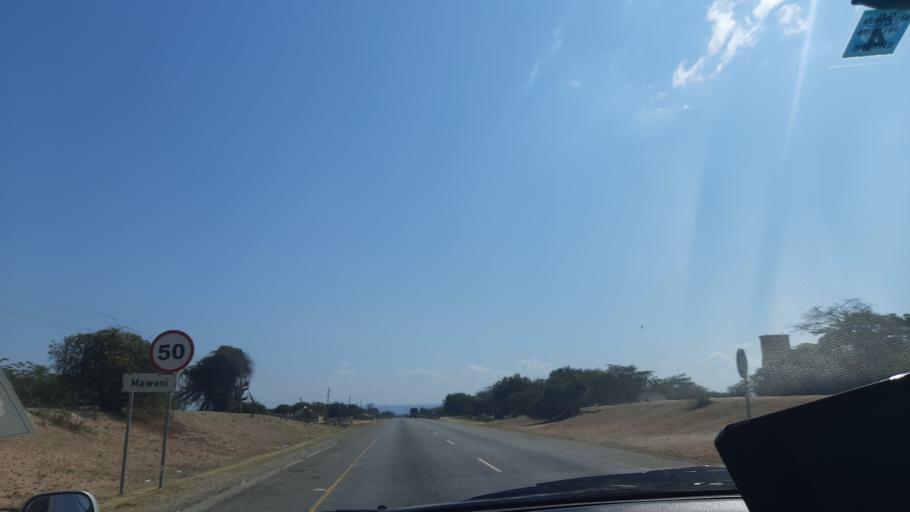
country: TZ
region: Singida
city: Kintinku
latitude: -5.8793
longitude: 35.1279
